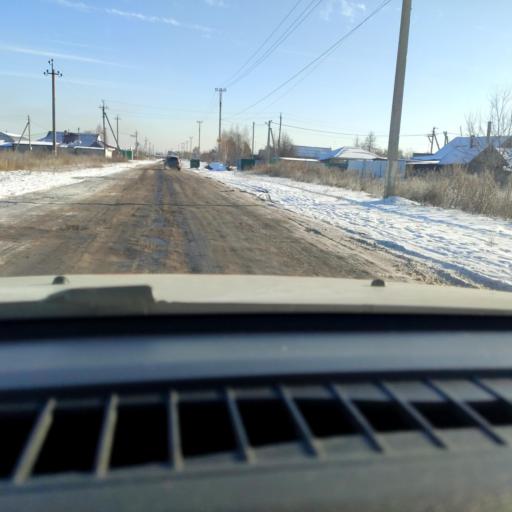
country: RU
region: Samara
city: Podstepki
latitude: 53.5194
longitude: 49.1347
